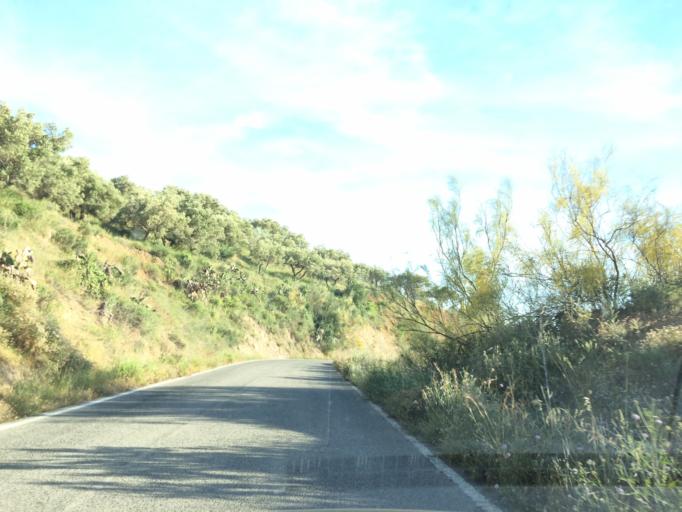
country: ES
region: Andalusia
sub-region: Provincia de Malaga
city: Totalan
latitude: 36.7384
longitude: -4.3316
